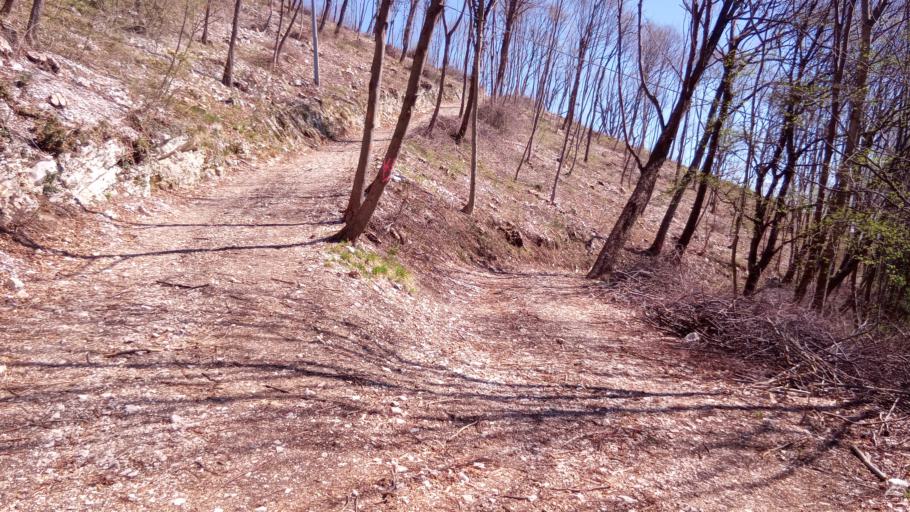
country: IT
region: Veneto
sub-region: Provincia di Treviso
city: Paderno del Grappa
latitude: 45.8613
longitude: 11.8453
